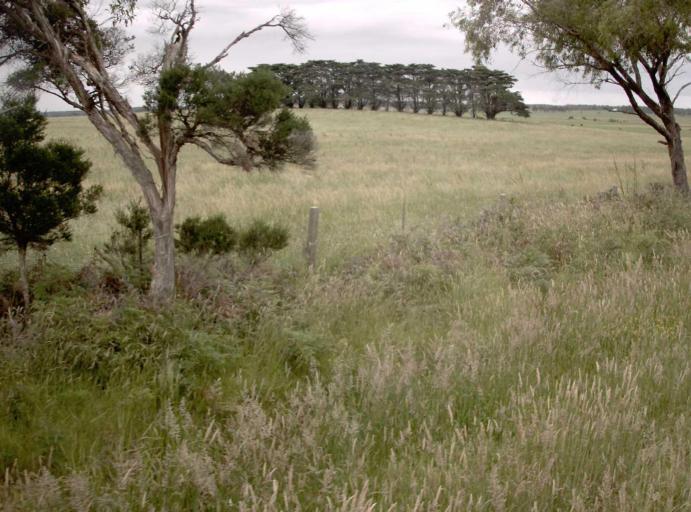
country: AU
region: Victoria
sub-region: Bass Coast
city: North Wonthaggi
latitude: -38.5443
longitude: 145.6972
